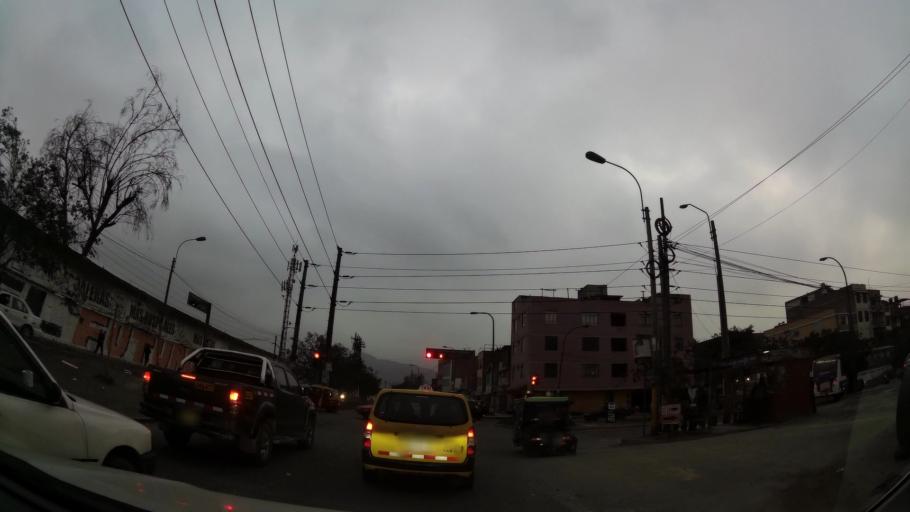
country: PE
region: Lima
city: Lima
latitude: -12.0167
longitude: -76.9970
